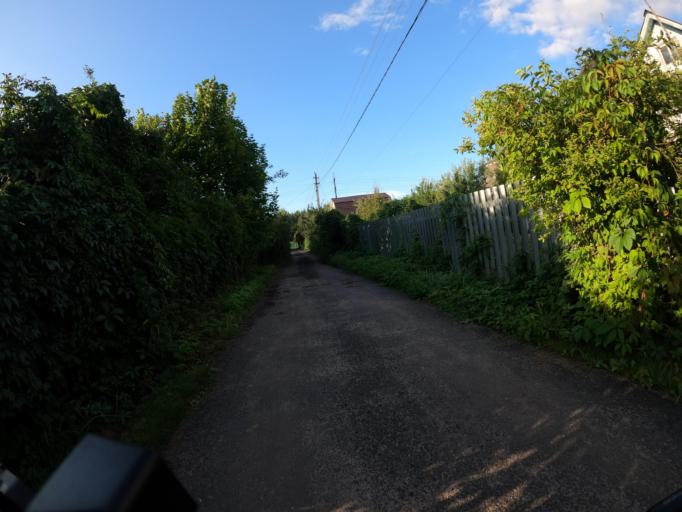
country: RU
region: Moskovskaya
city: Beloozerskiy
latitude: 55.4506
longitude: 38.5007
